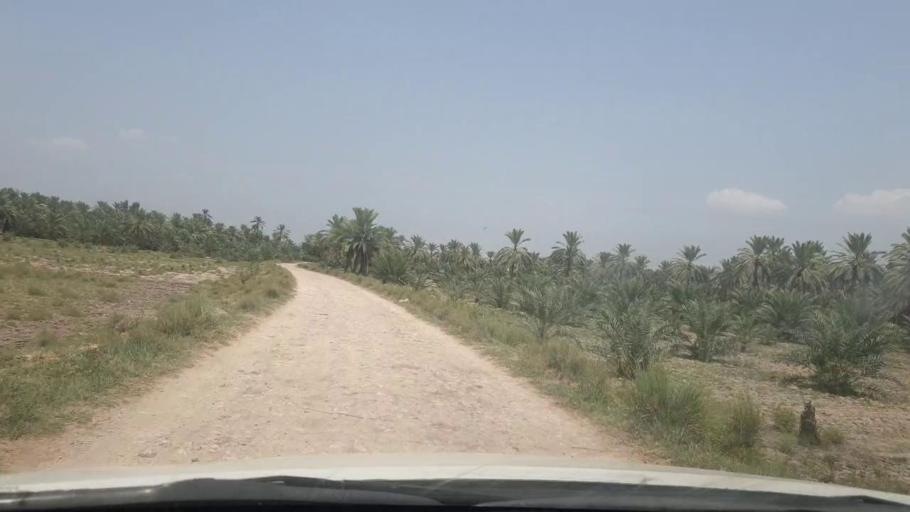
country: PK
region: Sindh
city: Khairpur
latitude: 27.5477
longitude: 68.8278
